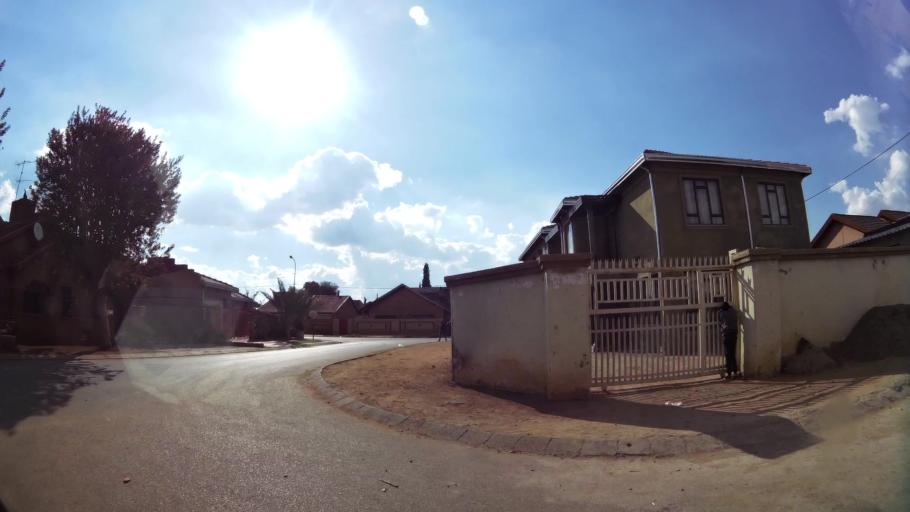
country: ZA
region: Gauteng
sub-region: City of Johannesburg Metropolitan Municipality
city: Soweto
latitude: -26.2226
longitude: 27.8623
